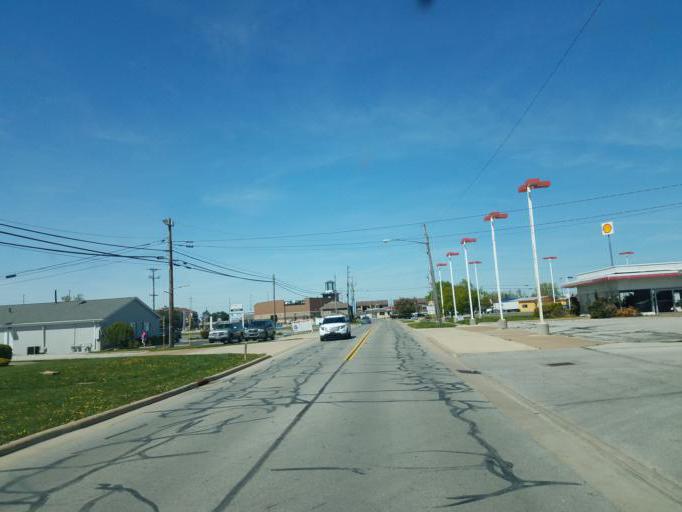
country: US
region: Ohio
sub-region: Ottawa County
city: Port Clinton
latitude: 41.5126
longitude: -82.9131
